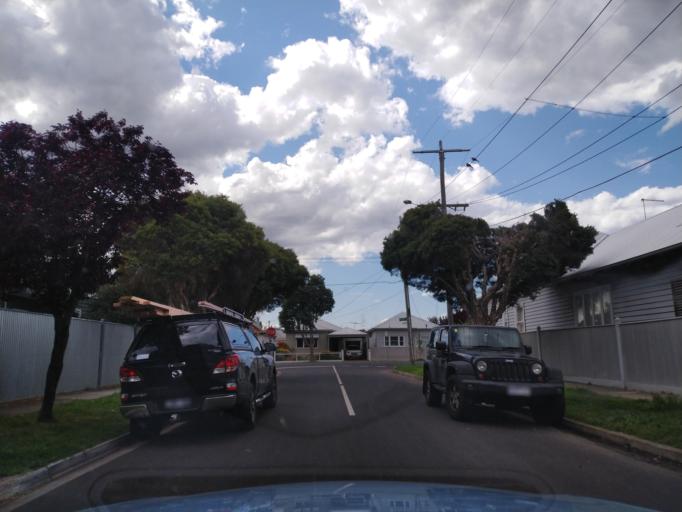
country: AU
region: Victoria
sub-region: Hobsons Bay
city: Newport
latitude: -37.8462
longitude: 144.8779
